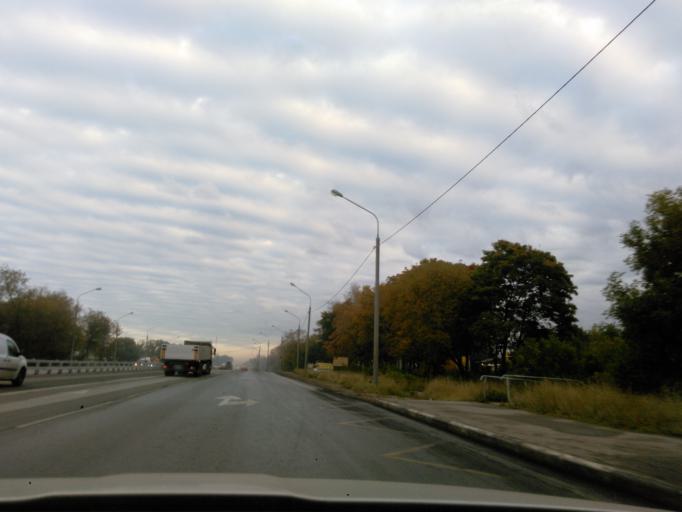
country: RU
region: Moskovskaya
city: Novopodrezkovo
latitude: 55.9421
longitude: 37.3627
